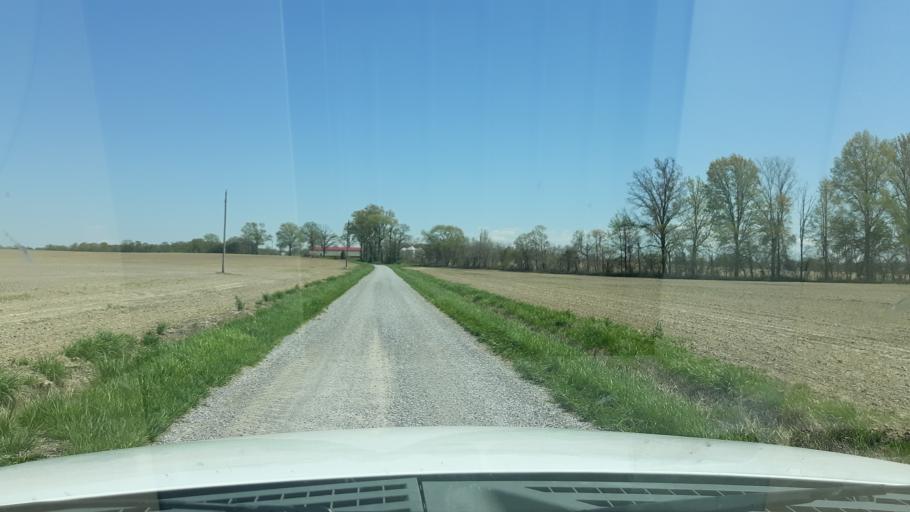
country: US
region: Illinois
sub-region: Saline County
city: Harrisburg
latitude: 37.8897
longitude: -88.6788
